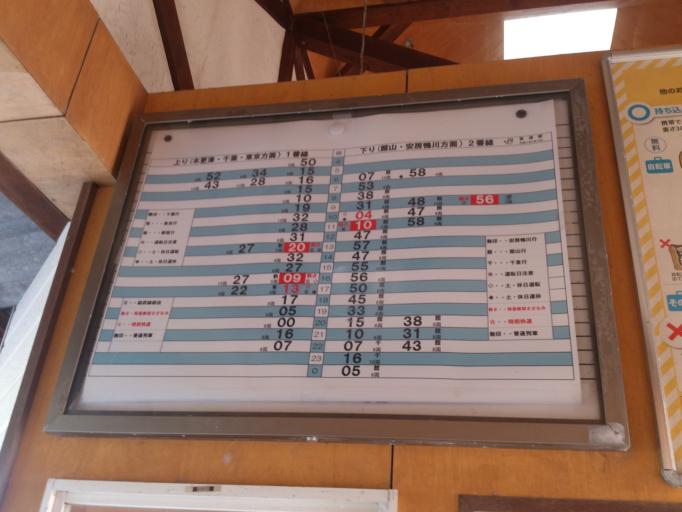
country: JP
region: Chiba
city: Tateyama
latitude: 35.0454
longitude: 139.8377
